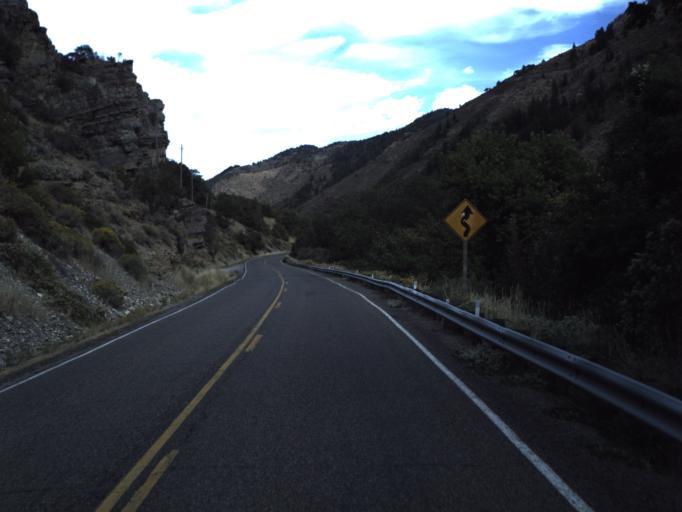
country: US
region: Utah
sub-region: Cache County
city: Millville
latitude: 41.6213
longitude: -111.7529
